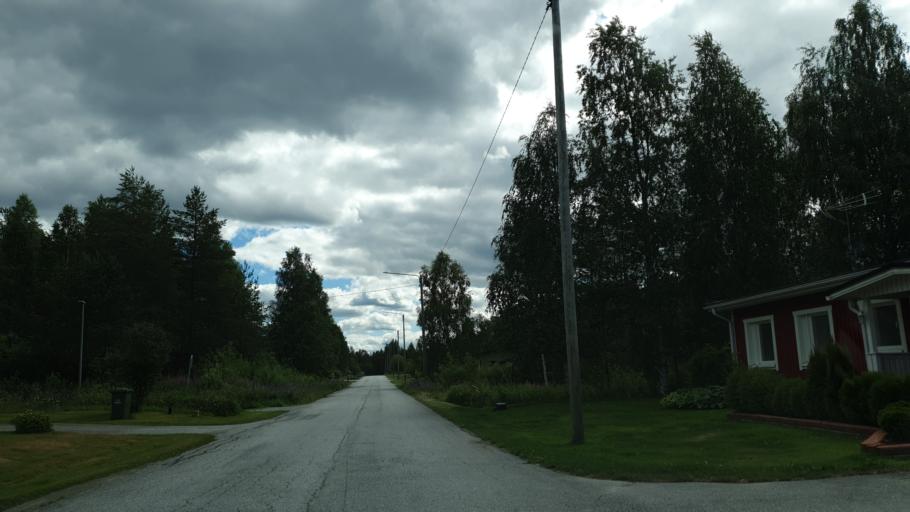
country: FI
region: Kainuu
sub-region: Kehys-Kainuu
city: Kuhmo
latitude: 64.1138
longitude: 29.4818
